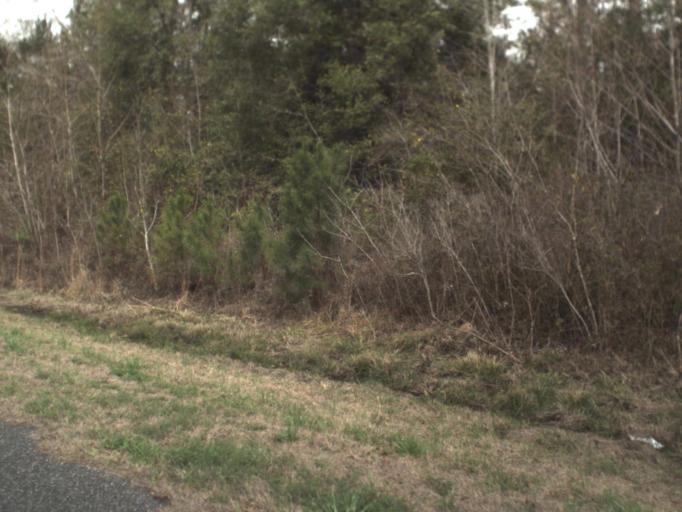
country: US
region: Florida
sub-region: Leon County
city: Woodville
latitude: 30.4115
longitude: -84.0710
